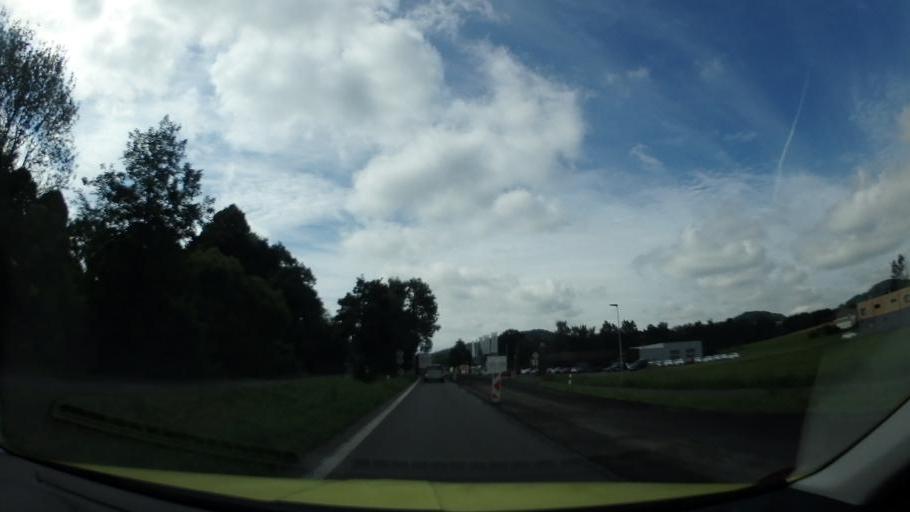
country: CZ
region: Moravskoslezsky
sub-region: Okres Novy Jicin
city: Novy Jicin
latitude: 49.5817
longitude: 18.0226
